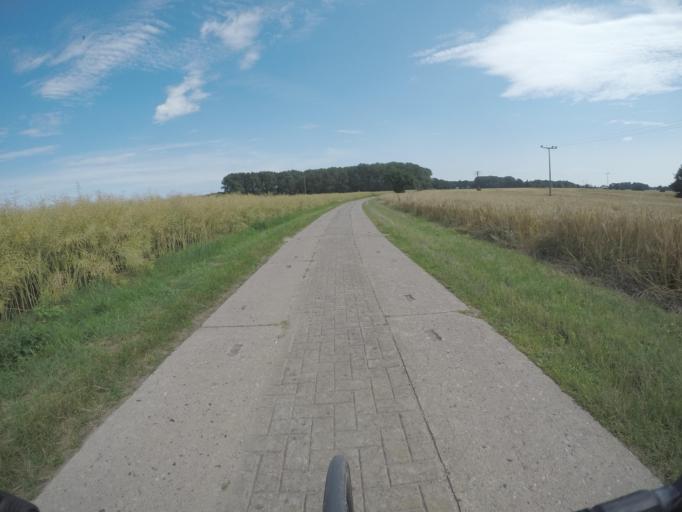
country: DE
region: Mecklenburg-Vorpommern
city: Altefahr
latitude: 54.3686
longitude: 13.1560
